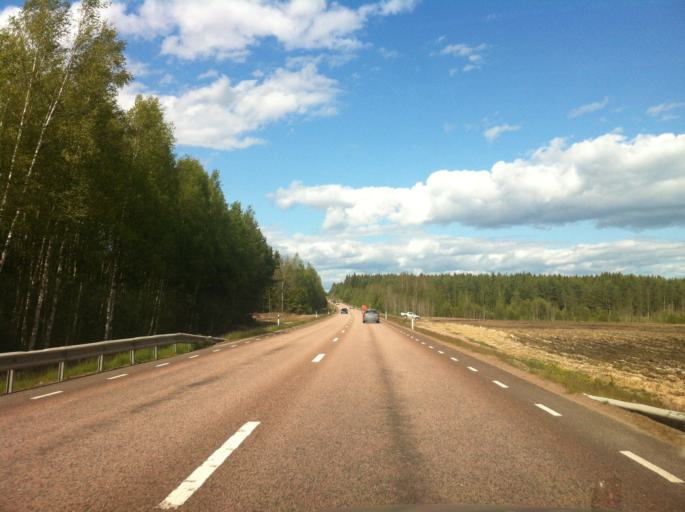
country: SE
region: Vaermland
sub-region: Kristinehamns Kommun
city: Kristinehamn
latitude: 59.3432
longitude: 14.1304
